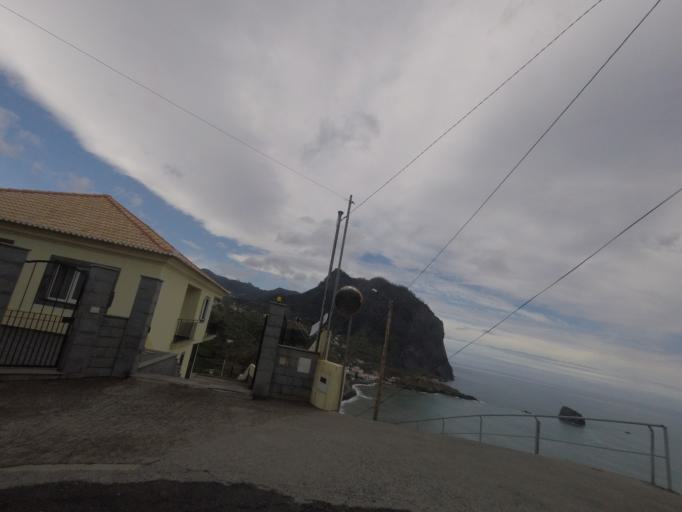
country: PT
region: Madeira
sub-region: Santana
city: Santana
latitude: 32.7660
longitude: -16.8189
